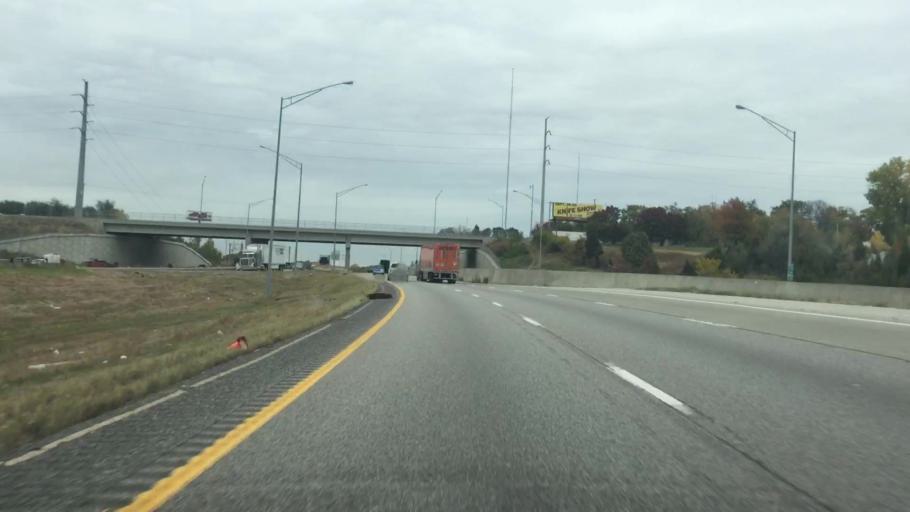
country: US
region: Missouri
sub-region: Jackson County
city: Raytown
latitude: 39.0612
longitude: -94.4883
